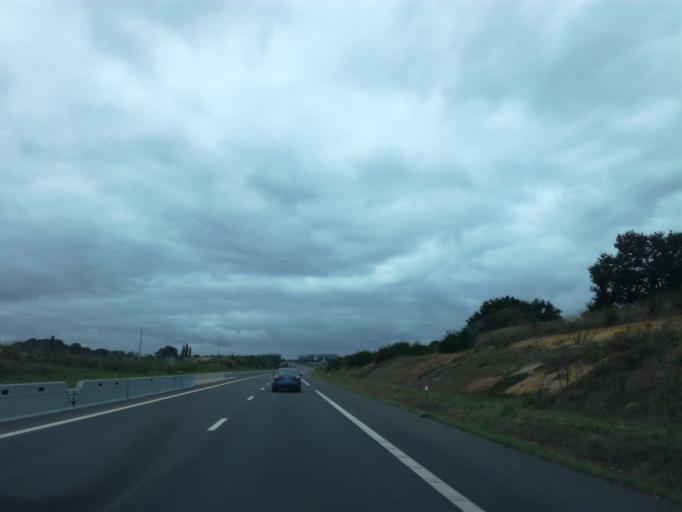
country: FR
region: Brittany
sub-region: Departement d'Ille-et-Vilaine
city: Boisgervilly
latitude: 48.1907
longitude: -2.1215
